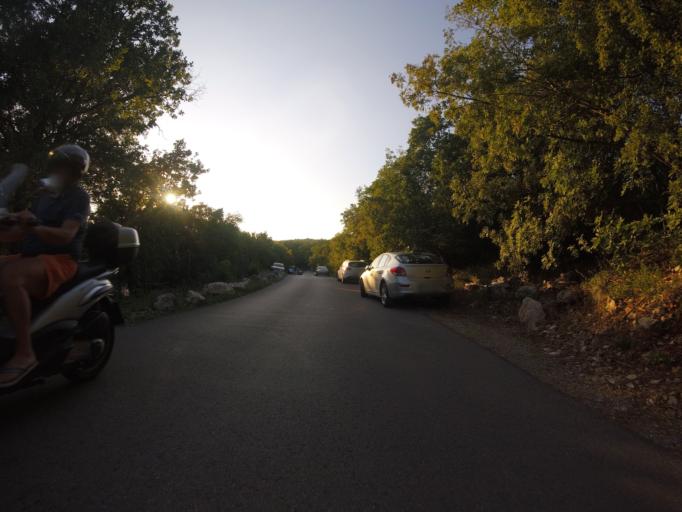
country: HR
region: Primorsko-Goranska
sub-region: Grad Crikvenica
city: Jadranovo
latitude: 45.2037
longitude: 14.6521
